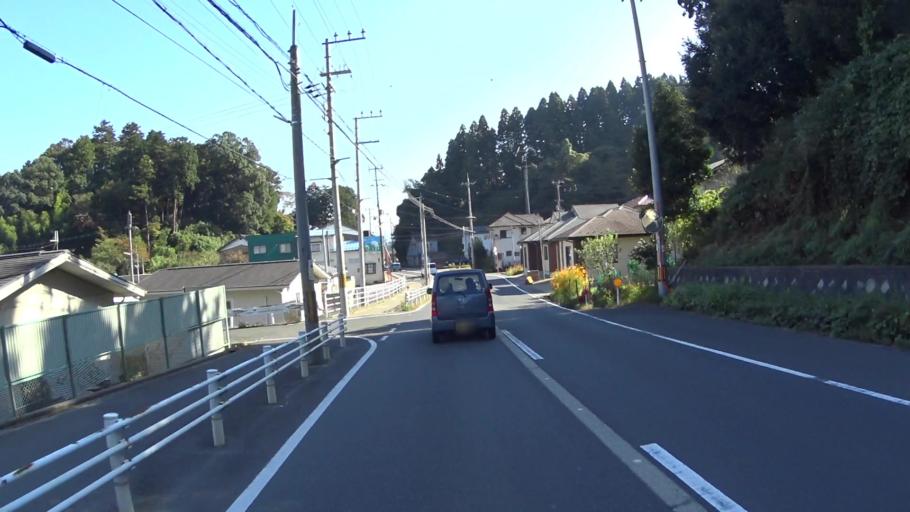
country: JP
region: Kyoto
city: Miyazu
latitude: 35.6322
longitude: 135.0545
